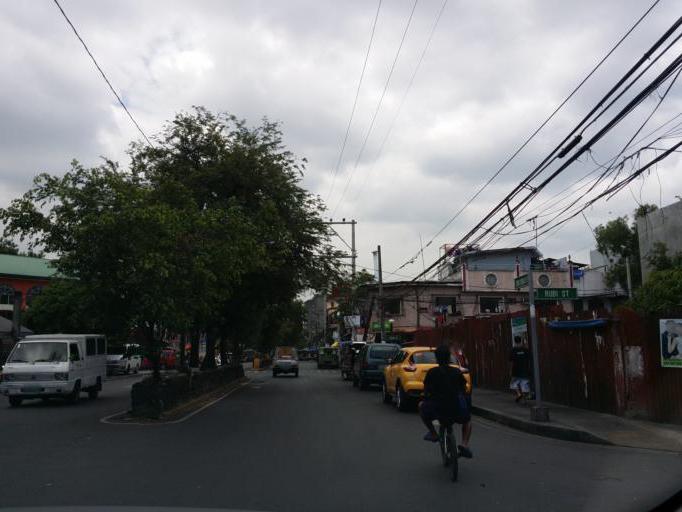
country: PH
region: Metro Manila
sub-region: Makati City
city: Makati City
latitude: 14.5688
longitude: 121.0058
